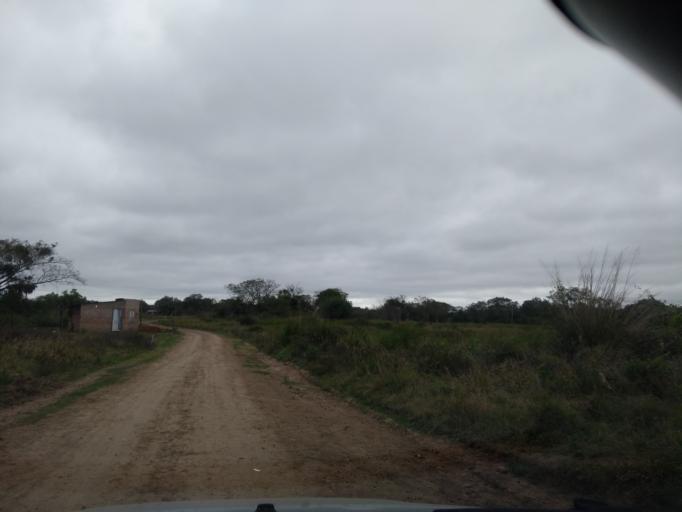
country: AR
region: Chaco
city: Barranqueras
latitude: -27.4372
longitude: -58.9389
